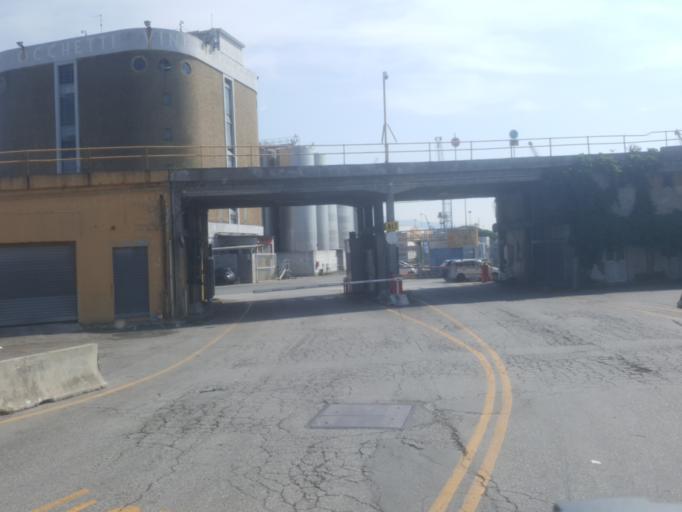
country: IT
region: Liguria
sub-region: Provincia di Genova
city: San Teodoro
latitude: 44.4068
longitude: 8.8900
